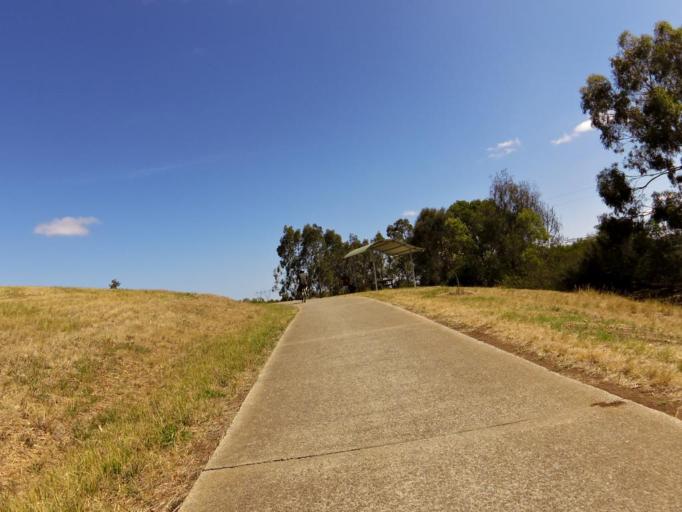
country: AU
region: Victoria
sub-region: Hume
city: Meadow Heights
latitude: -37.6587
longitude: 144.9083
